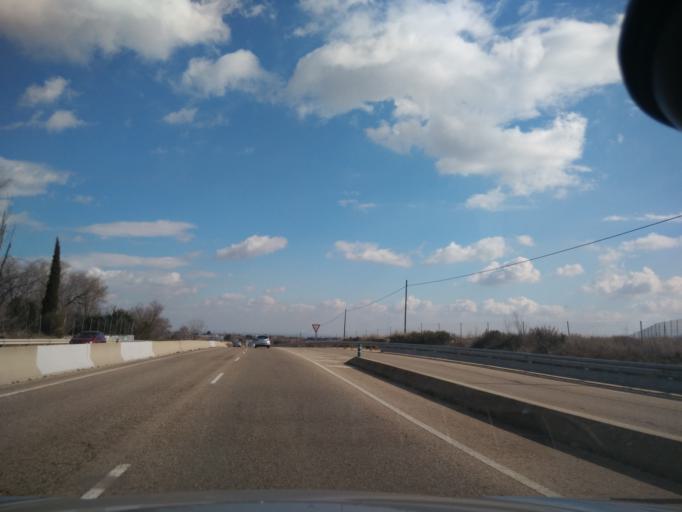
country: ES
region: Madrid
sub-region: Provincia de Madrid
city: Alcobendas
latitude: 40.5517
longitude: -3.6704
